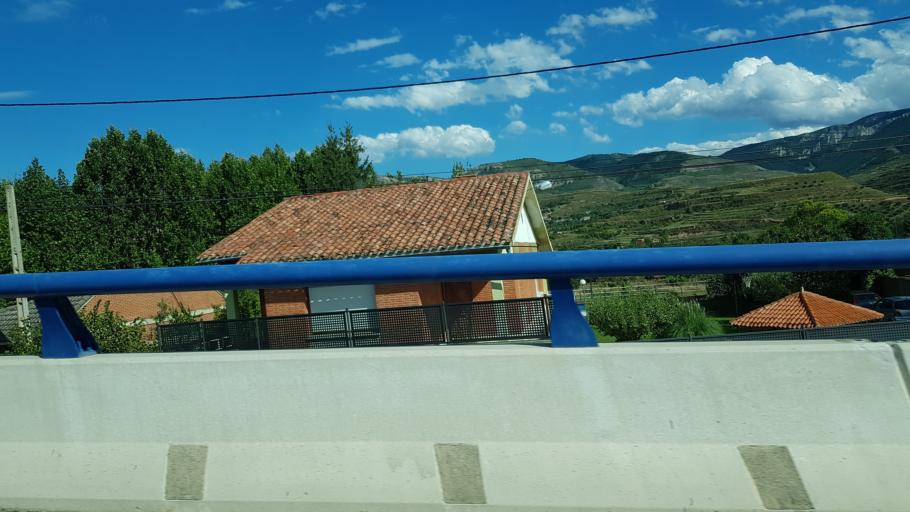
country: ES
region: La Rioja
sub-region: Provincia de La Rioja
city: Nalda
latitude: 42.3382
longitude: -2.5039
